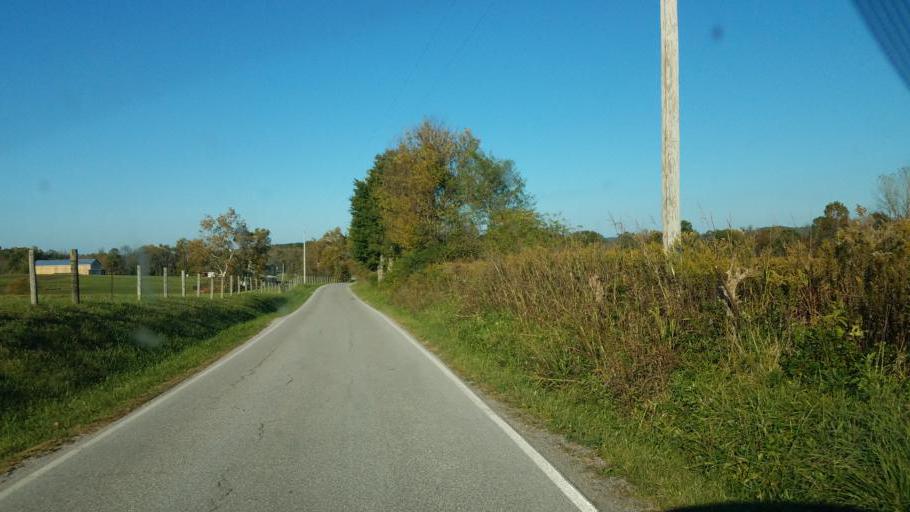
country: US
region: Kentucky
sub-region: Fleming County
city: Flemingsburg
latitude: 38.4852
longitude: -83.5975
